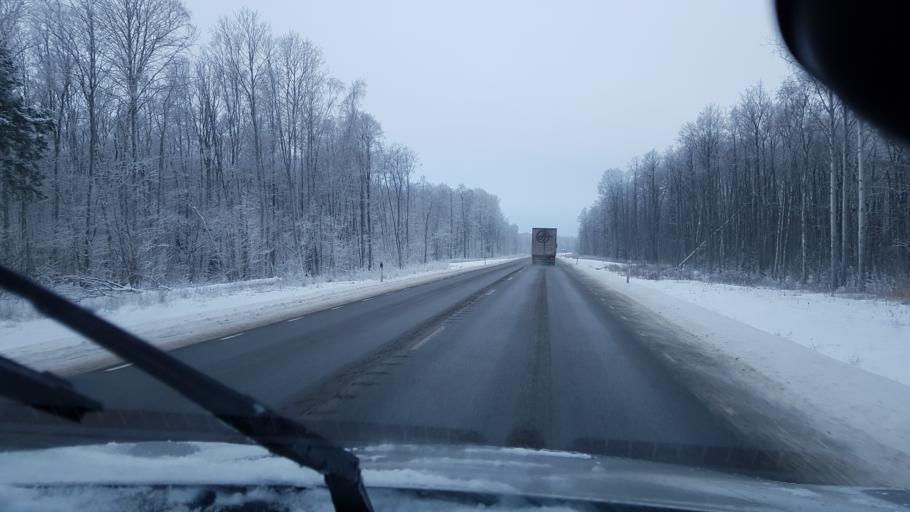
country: EE
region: Harju
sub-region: Paldiski linn
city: Paldiski
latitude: 59.3397
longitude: 24.1305
